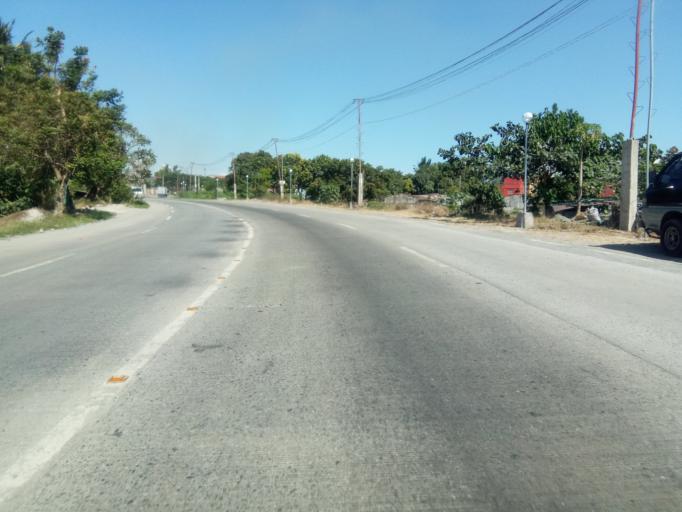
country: PH
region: Calabarzon
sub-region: Province of Cavite
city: Bulihan
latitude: 14.3084
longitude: 120.9897
